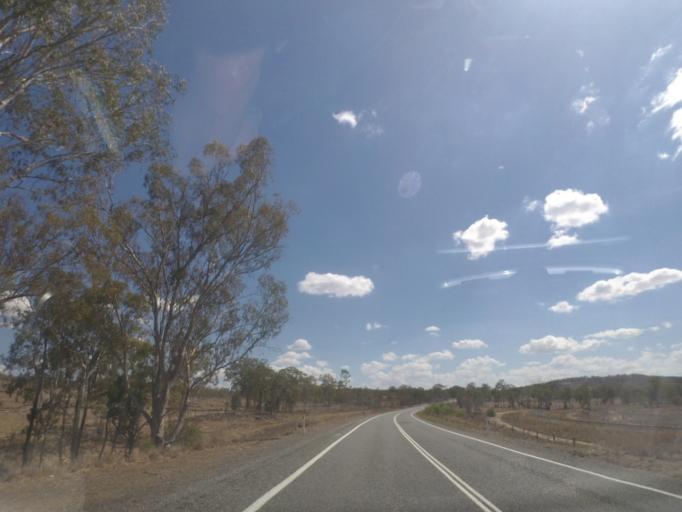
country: AU
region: Queensland
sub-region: Southern Downs
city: Warwick
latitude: -28.2162
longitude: 151.5622
